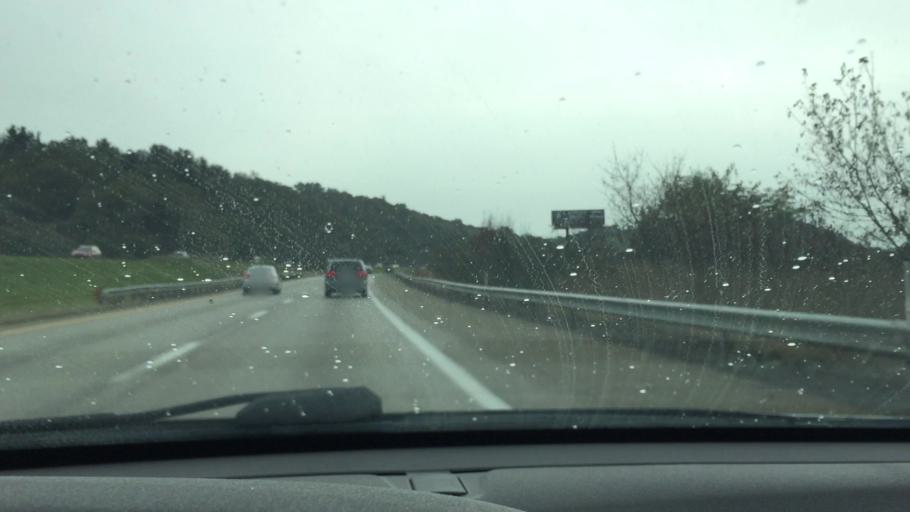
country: US
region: Pennsylvania
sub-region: Washington County
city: Canonsburg
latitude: 40.2750
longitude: -80.1591
